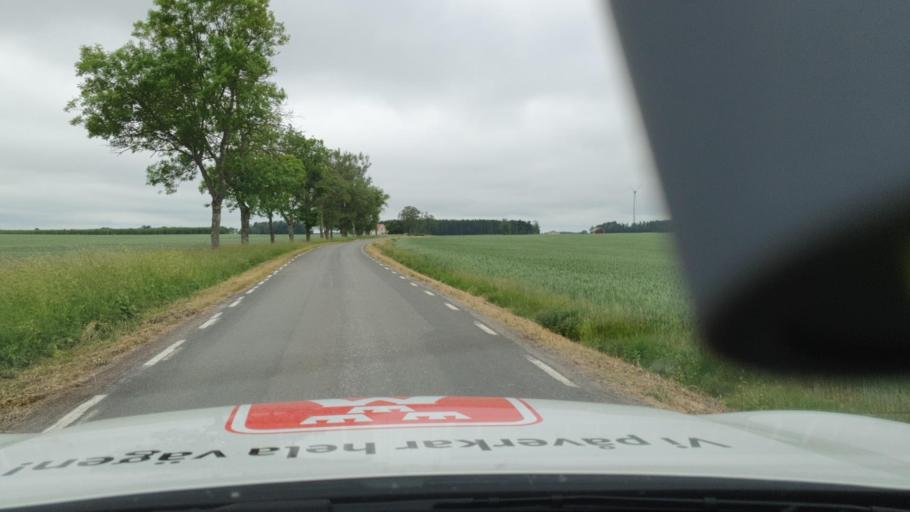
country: SE
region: Vaestra Goetaland
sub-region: Tibro Kommun
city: Tibro
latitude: 58.3681
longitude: 14.0942
